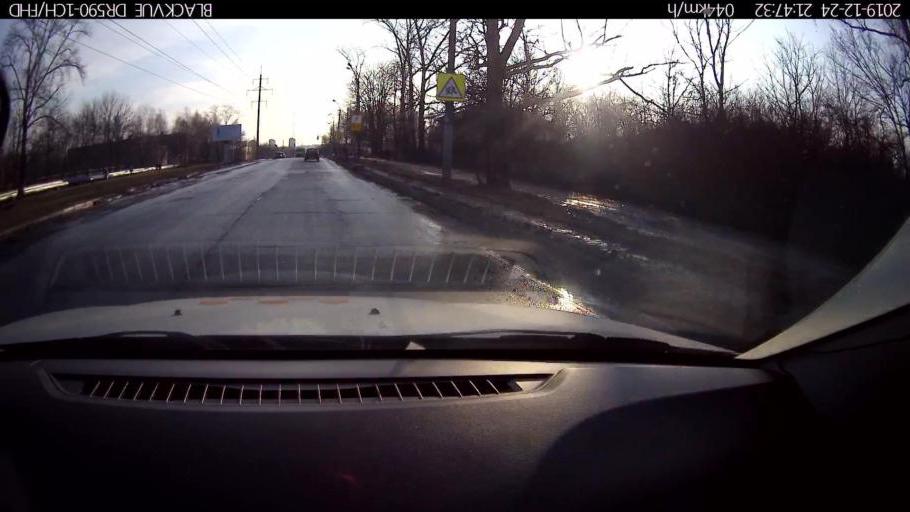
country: RU
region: Nizjnij Novgorod
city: Gorbatovka
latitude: 56.2299
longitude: 43.8410
